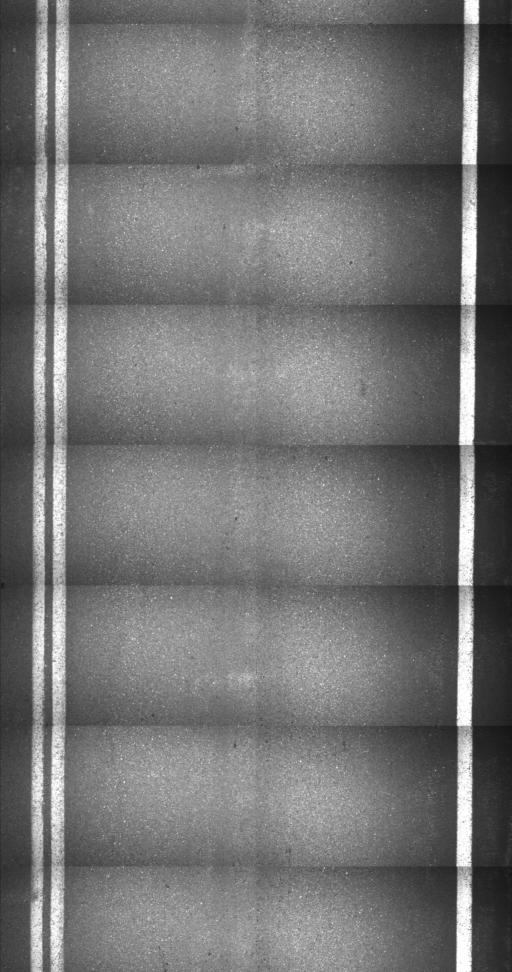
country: US
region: Vermont
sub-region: Caledonia County
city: Lyndonville
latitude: 44.7308
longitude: -71.8759
